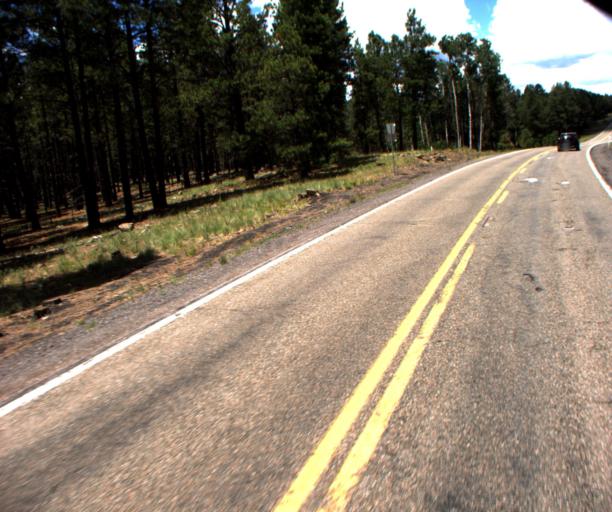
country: US
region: Arizona
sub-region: Coconino County
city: Parks
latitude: 35.3402
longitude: -111.7872
